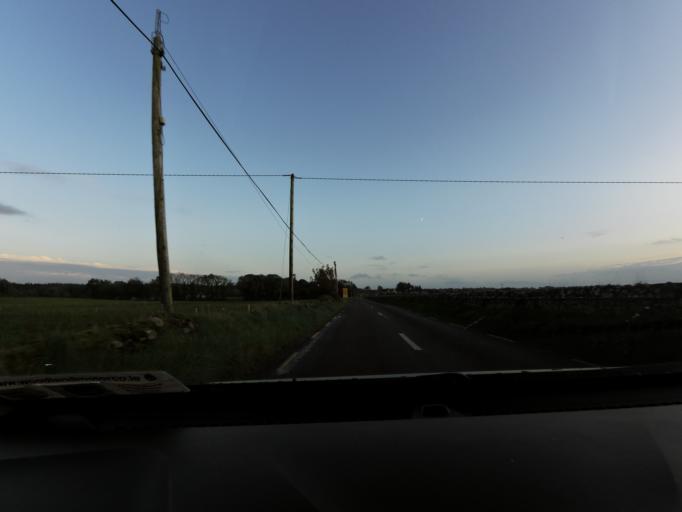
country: IE
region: Connaught
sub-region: County Galway
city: Tuam
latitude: 53.5198
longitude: -8.6184
